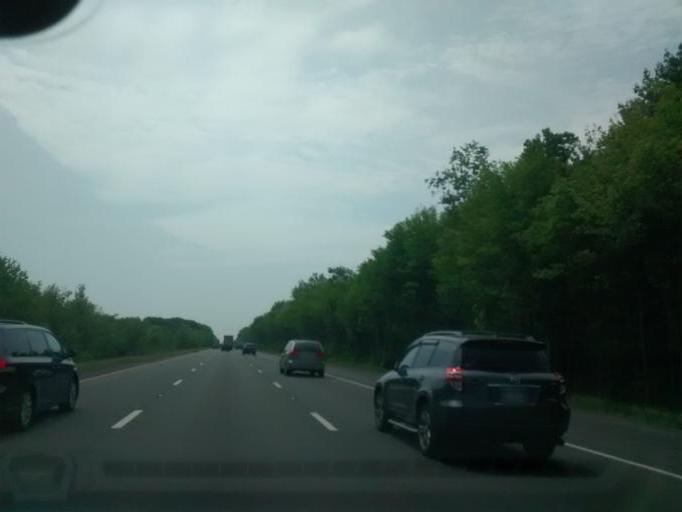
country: US
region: Massachusetts
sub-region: Worcester County
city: Milford
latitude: 42.1409
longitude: -71.4820
